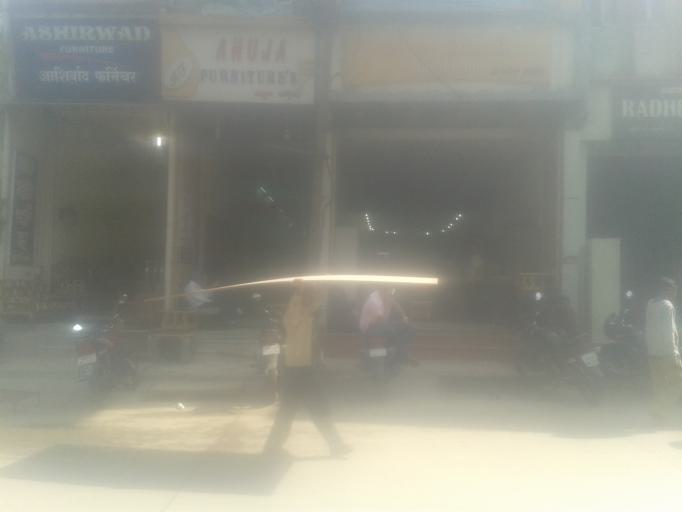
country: IN
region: Maharashtra
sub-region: Thane
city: Ulhasnagar
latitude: 19.2304
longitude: 73.1623
